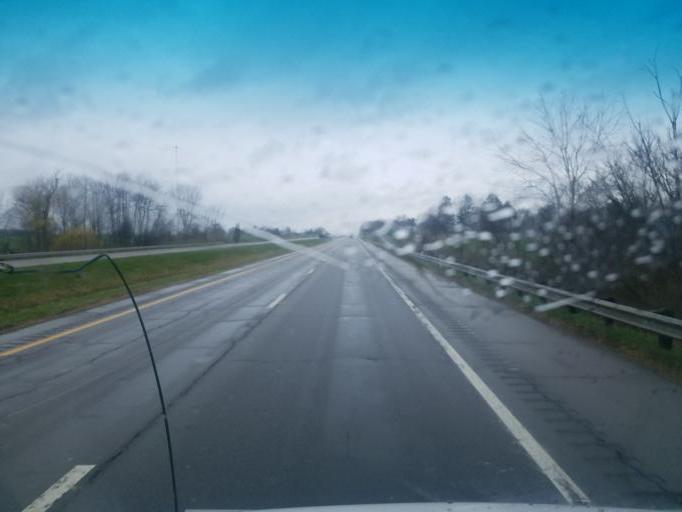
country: US
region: Ohio
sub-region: Wayne County
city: Wooster
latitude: 40.7998
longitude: -82.0195
